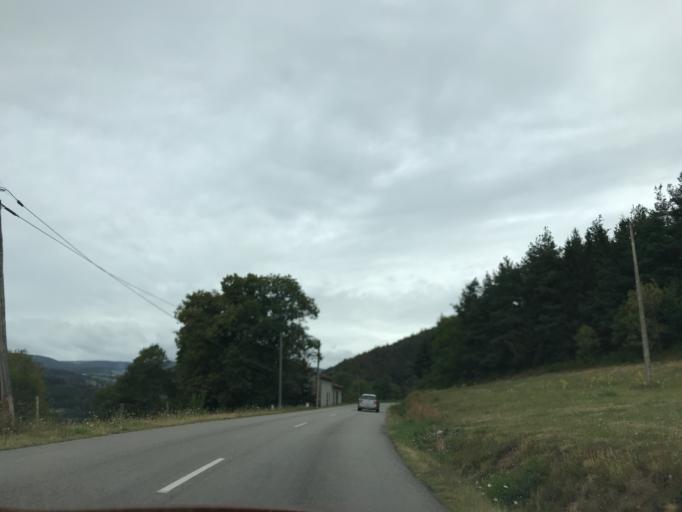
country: FR
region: Rhone-Alpes
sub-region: Departement de la Loire
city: Sail-sous-Couzan
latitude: 45.6911
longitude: 3.8941
